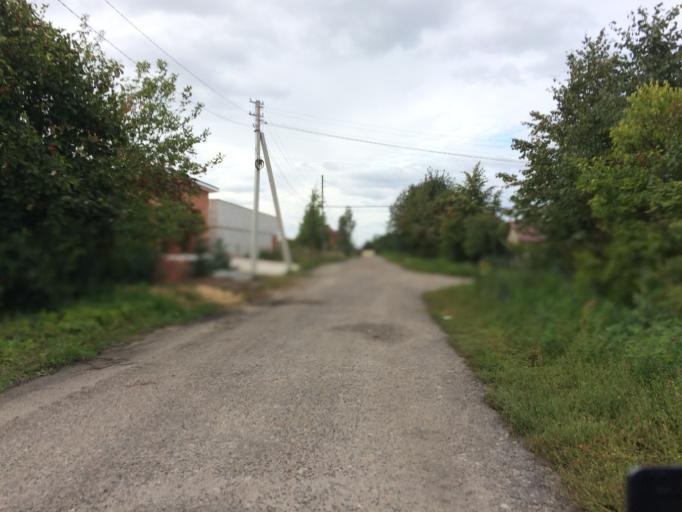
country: RU
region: Mariy-El
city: Yoshkar-Ola
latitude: 56.6615
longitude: 47.9936
